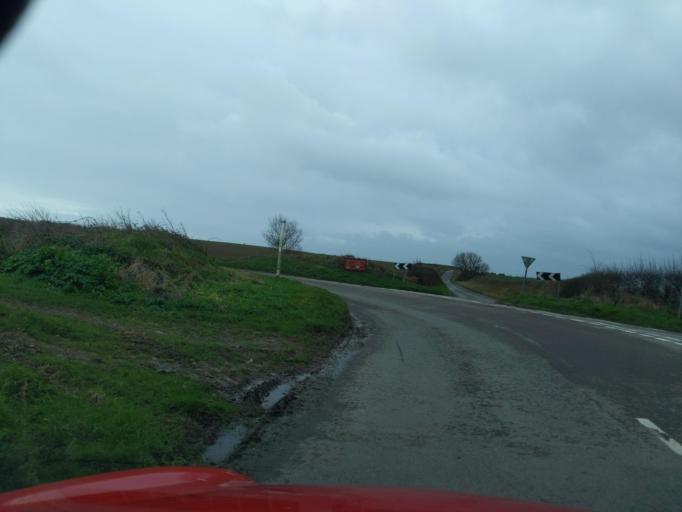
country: GB
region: England
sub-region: Devon
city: Modbury
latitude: 50.3261
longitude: -3.8858
